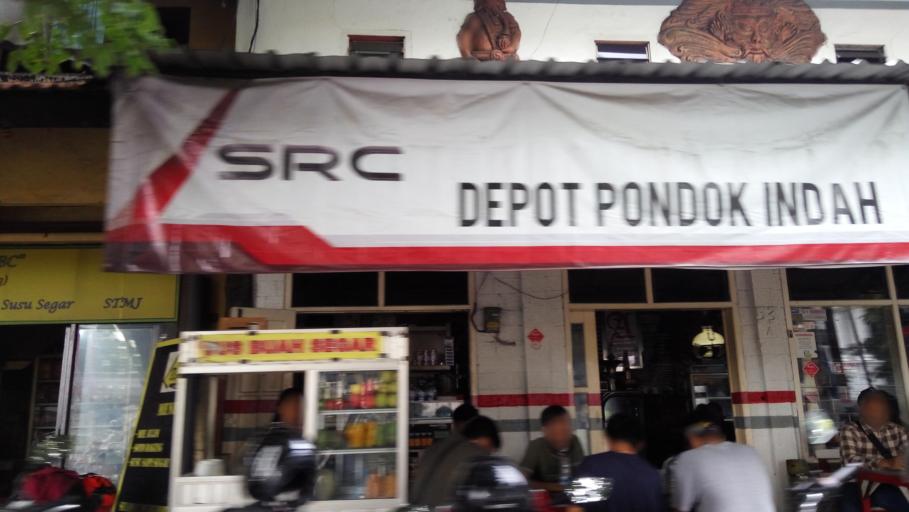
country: ID
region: East Java
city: Malang
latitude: -7.9221
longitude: 112.5957
